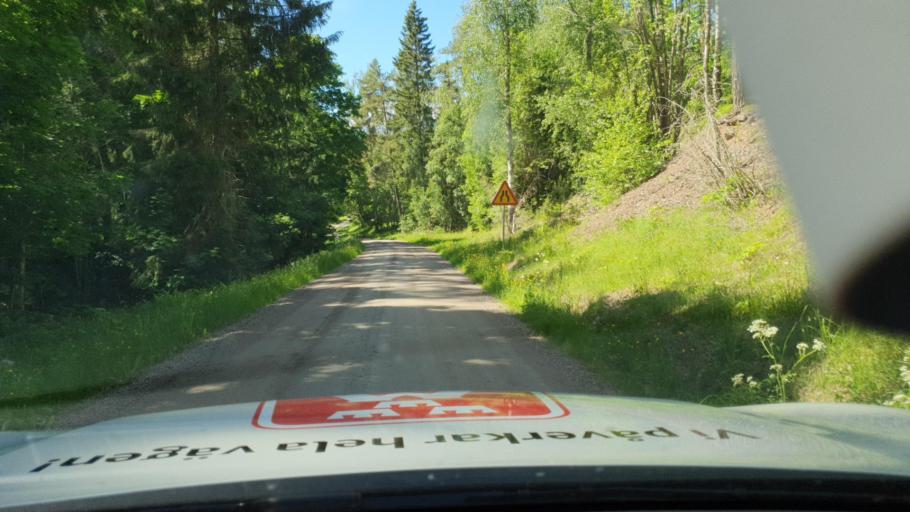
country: SE
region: Joenkoeping
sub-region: Mullsjo Kommun
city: Mullsjoe
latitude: 58.0386
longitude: 13.8684
